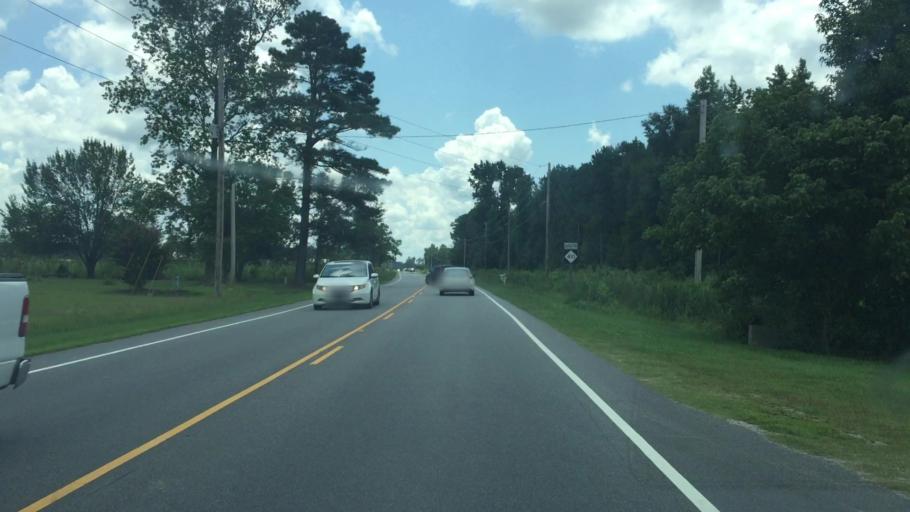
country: US
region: North Carolina
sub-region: Columbus County
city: Chadbourn
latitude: 34.2325
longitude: -78.8244
